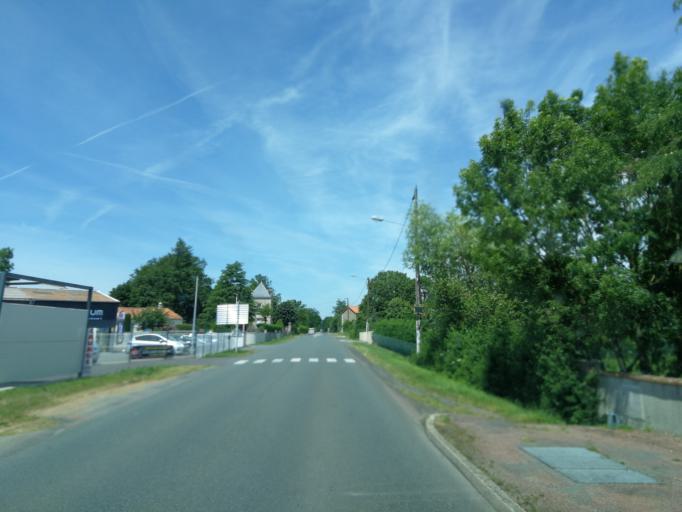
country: FR
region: Pays de la Loire
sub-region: Departement de la Vendee
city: Pissotte
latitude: 46.5279
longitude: -0.8075
